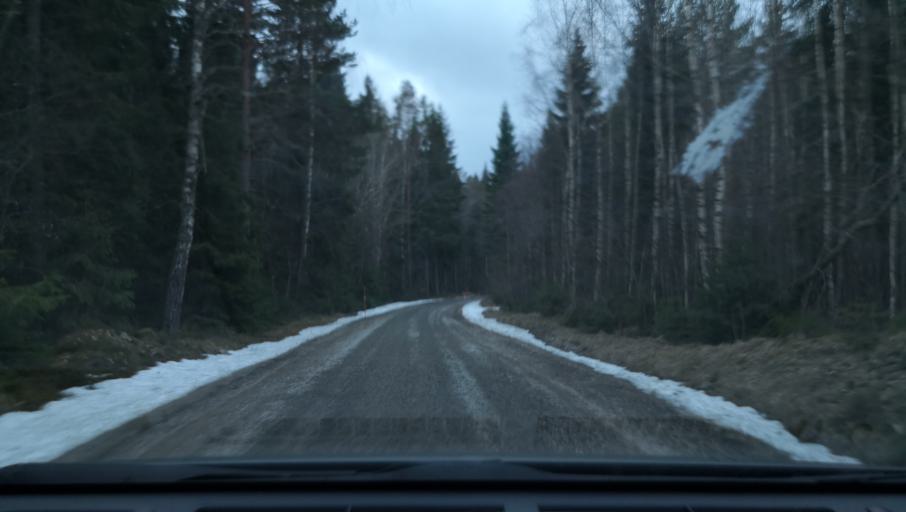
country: SE
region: OErebro
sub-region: Lindesbergs Kommun
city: Fellingsbro
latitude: 59.6019
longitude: 15.6486
